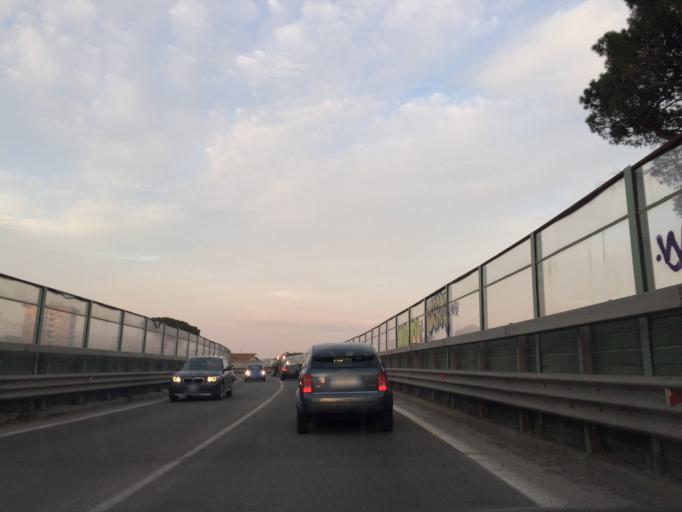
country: IT
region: Molise
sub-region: Provincia di Campobasso
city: Campobasso
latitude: 41.5577
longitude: 14.6751
